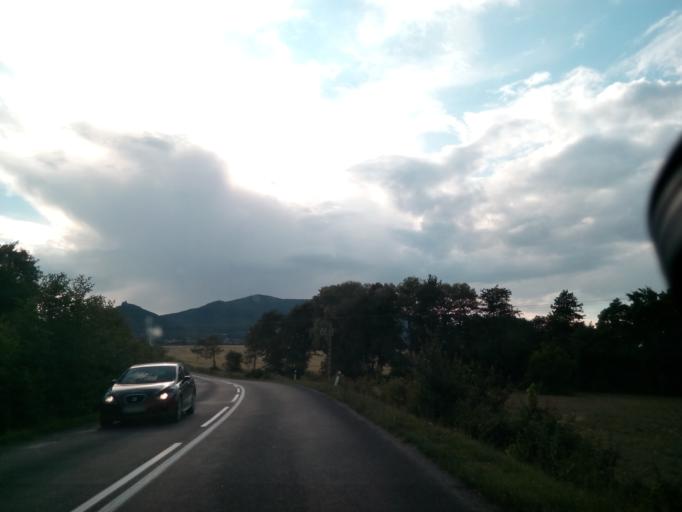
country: SK
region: Kosicky
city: Secovce
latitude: 48.6342
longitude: 21.5087
